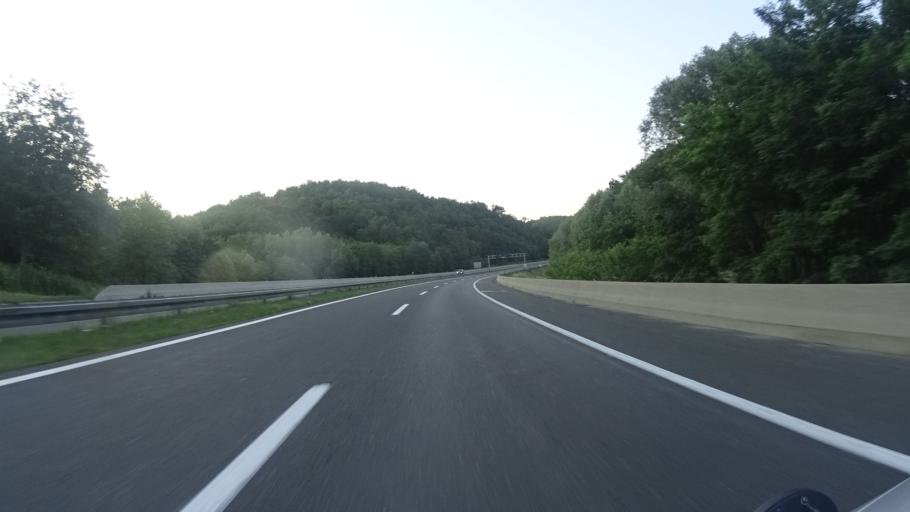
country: HR
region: Varazdinska
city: Ljubescica
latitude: 46.2140
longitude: 16.4043
